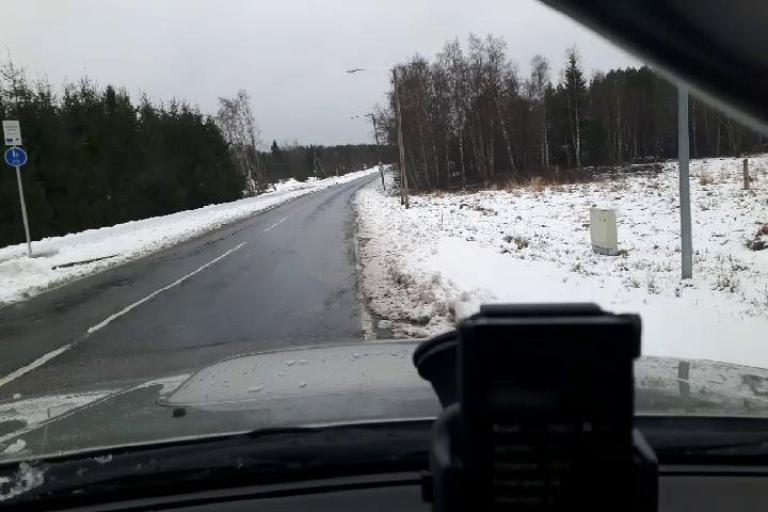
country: EE
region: Harju
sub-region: Harku vald
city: Tabasalu
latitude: 59.4374
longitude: 24.4991
